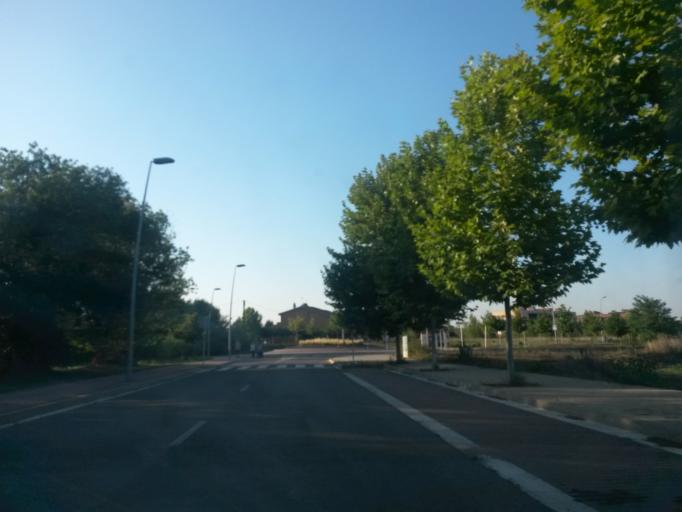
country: ES
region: Catalonia
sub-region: Provincia de Girona
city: Vilablareix
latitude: 41.9472
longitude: 2.7930
